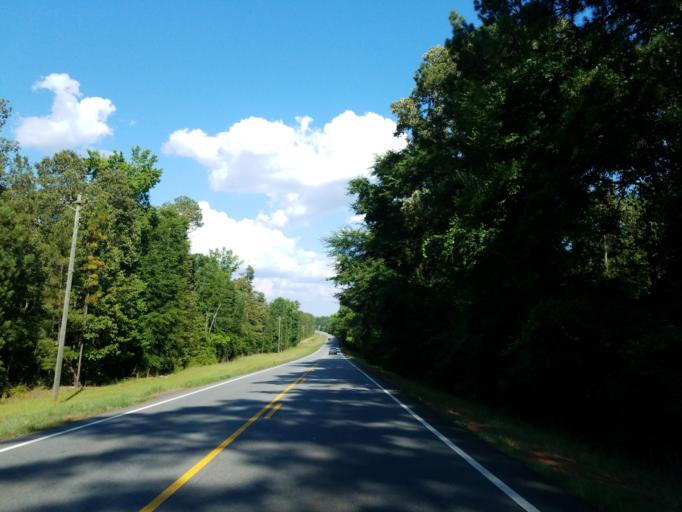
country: US
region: Georgia
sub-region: Houston County
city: Perry
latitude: 32.5513
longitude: -83.7731
